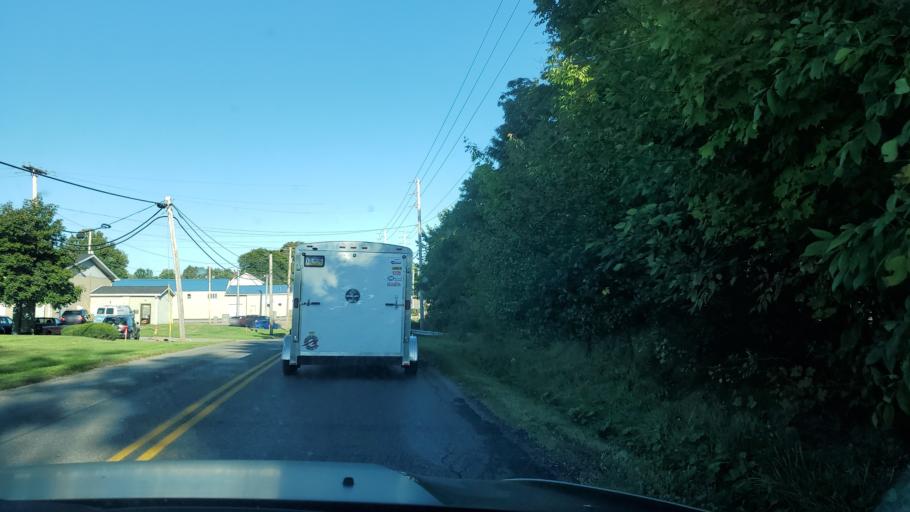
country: US
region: Ohio
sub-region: Mahoning County
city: Boardman
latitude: 40.9880
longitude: -80.6644
